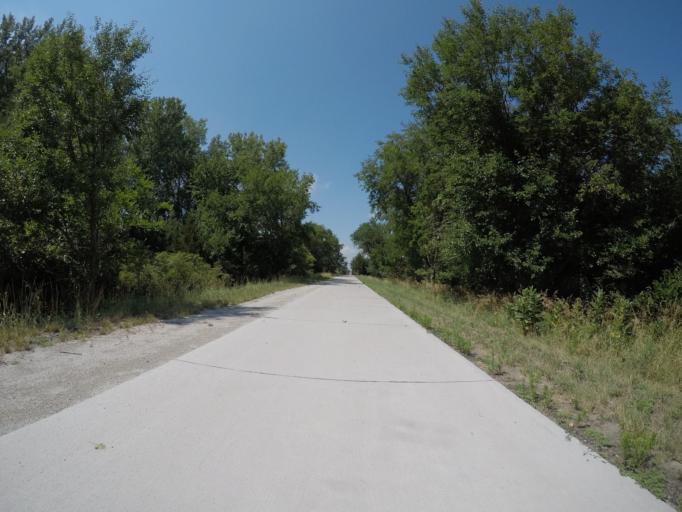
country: US
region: Nebraska
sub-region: Buffalo County
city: Kearney
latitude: 40.6591
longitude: -98.9869
